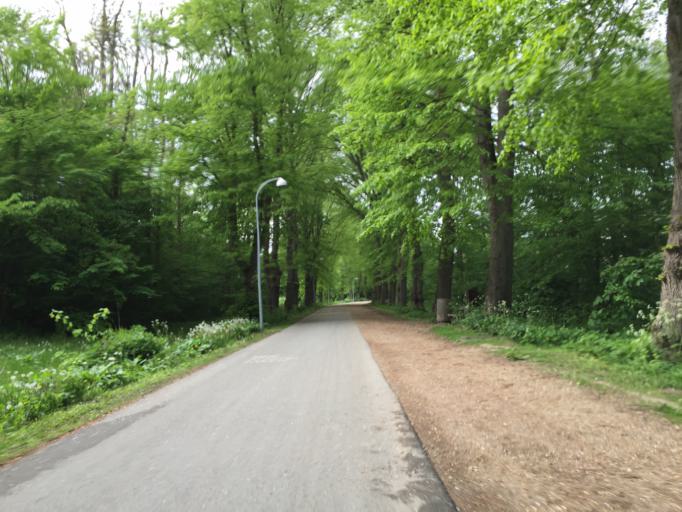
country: DK
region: Capital Region
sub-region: Brondby Kommune
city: Brondbyvester
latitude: 55.6245
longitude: 12.4440
